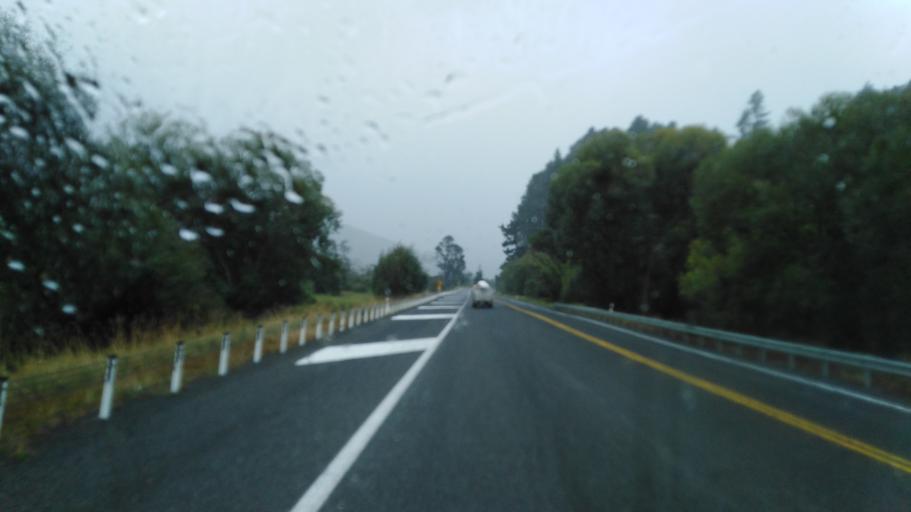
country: NZ
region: Marlborough
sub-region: Marlborough District
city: Picton
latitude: -41.3771
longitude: 173.9468
